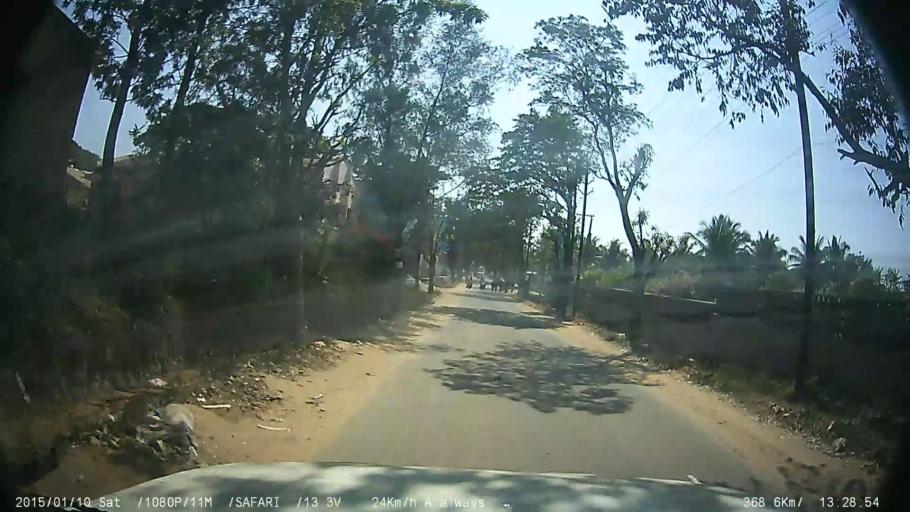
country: IN
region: Tamil Nadu
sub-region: Krishnagiri
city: Hosur
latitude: 12.7716
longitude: 77.7975
